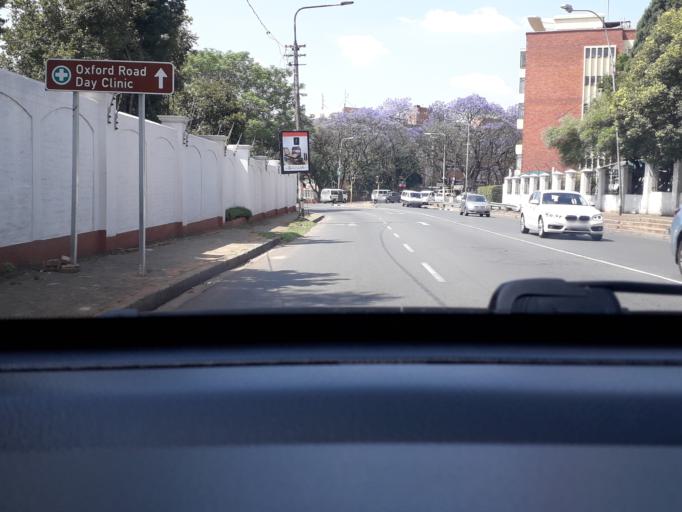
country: ZA
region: Gauteng
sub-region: City of Johannesburg Metropolitan Municipality
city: Johannesburg
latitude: -26.1655
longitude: 28.0474
